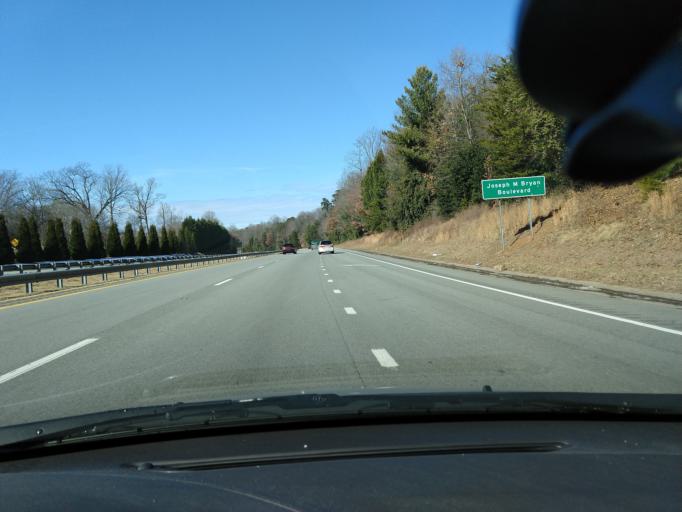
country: US
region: North Carolina
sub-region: Guilford County
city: Greensboro
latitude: 36.1155
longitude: -79.8554
